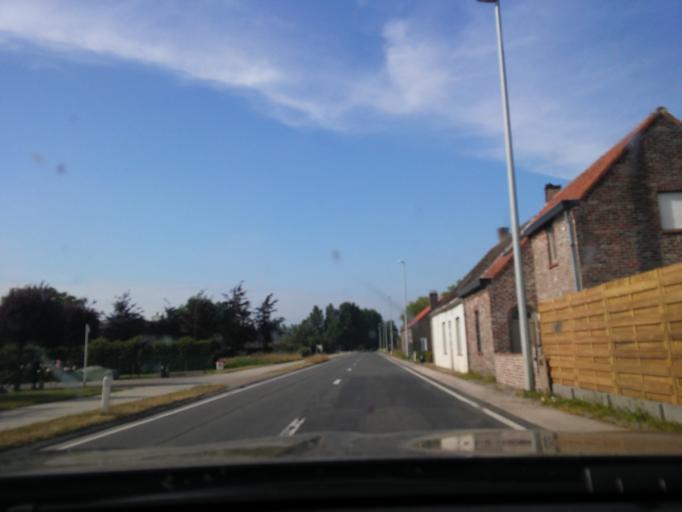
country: BE
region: Flanders
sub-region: Provincie Oost-Vlaanderen
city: Kaprijke
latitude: 51.2338
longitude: 3.5911
